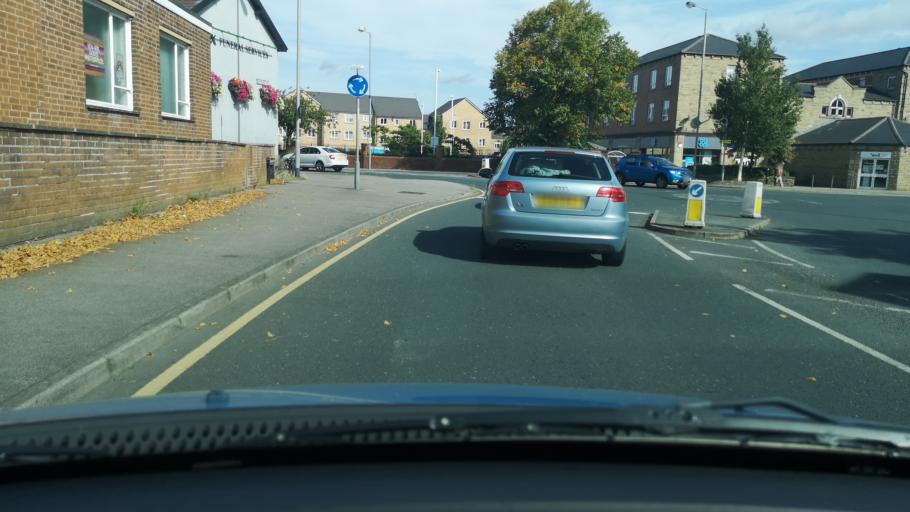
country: GB
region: England
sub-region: City and Borough of Wakefield
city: Ossett
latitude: 53.6800
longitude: -1.5807
